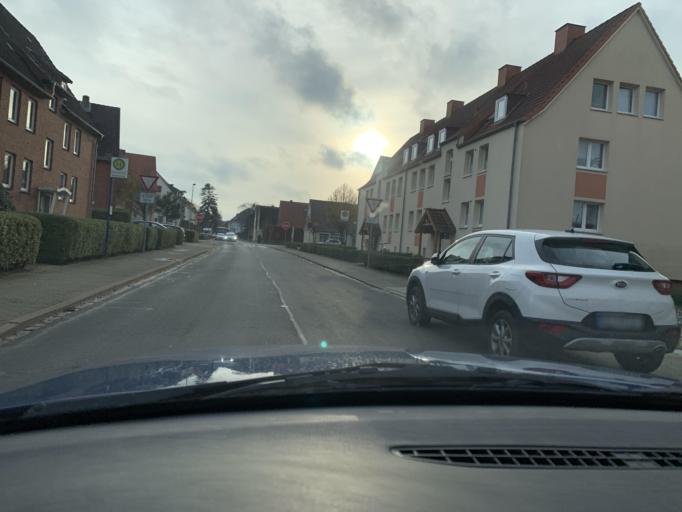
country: DE
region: Schleswig-Holstein
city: Wesseln
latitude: 54.2007
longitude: 9.0863
